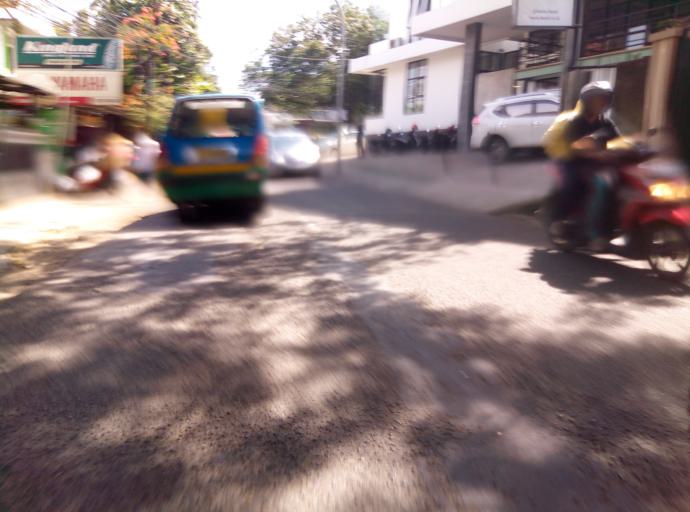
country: ID
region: West Java
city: Bandung
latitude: -6.8879
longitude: 107.6243
